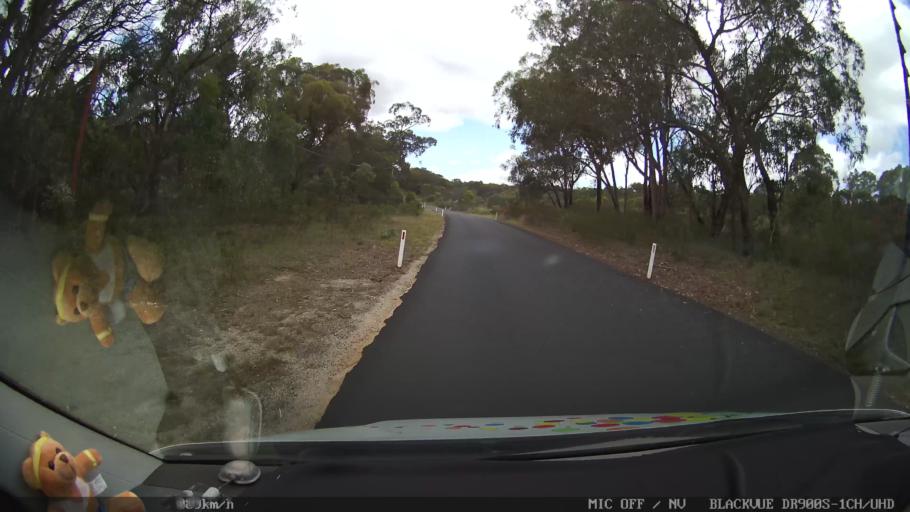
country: AU
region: New South Wales
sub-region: Glen Innes Severn
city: Glen Innes
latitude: -29.4382
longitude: 151.6277
